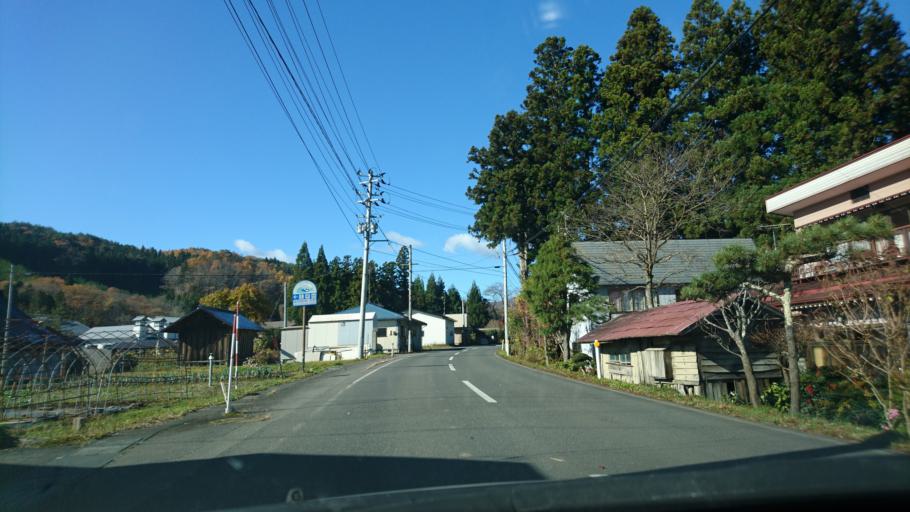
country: JP
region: Iwate
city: Mizusawa
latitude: 39.1165
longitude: 140.9458
